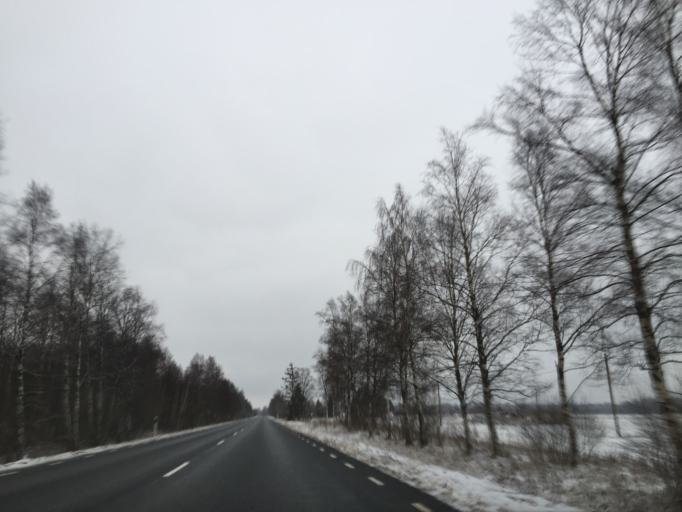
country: EE
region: Laeaene
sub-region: Lihula vald
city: Lihula
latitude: 58.6428
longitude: 23.8523
